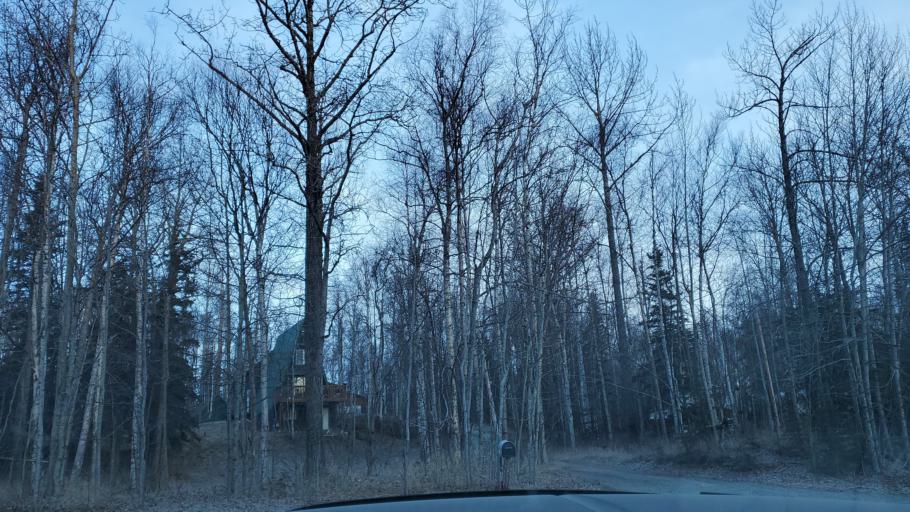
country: US
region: Alaska
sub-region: Matanuska-Susitna Borough
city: Lakes
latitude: 61.6031
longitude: -149.3237
